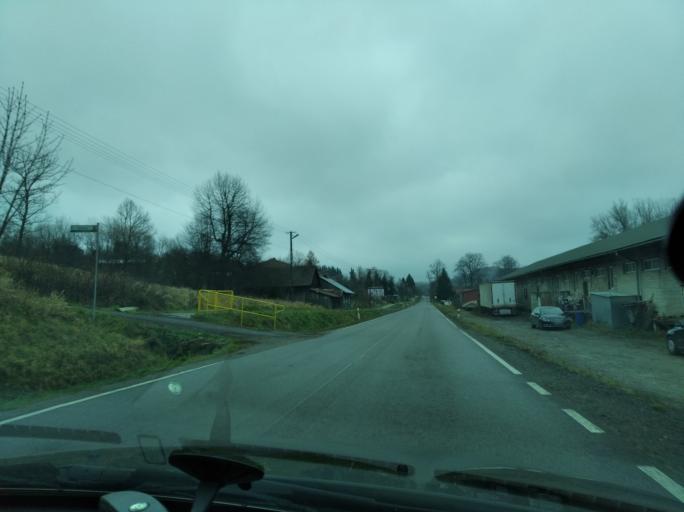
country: PL
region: Subcarpathian Voivodeship
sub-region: Powiat przeworski
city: Jawornik Polski
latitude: 49.8897
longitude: 22.2716
